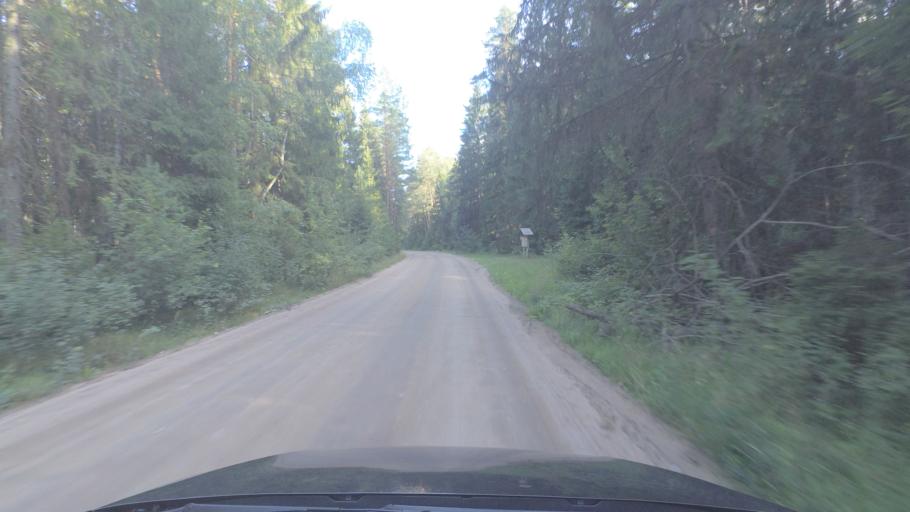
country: LT
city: Svencioneliai
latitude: 55.1651
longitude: 25.8419
